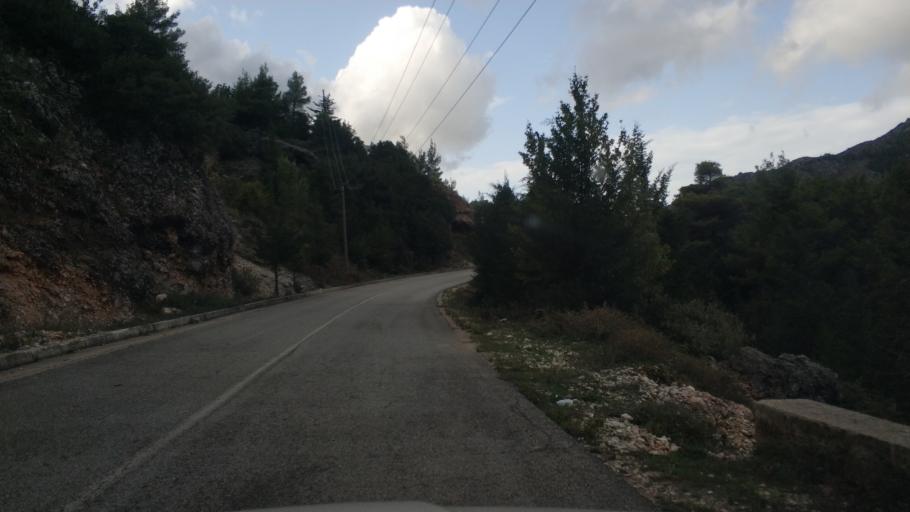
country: AL
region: Vlore
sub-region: Rrethi i Vlores
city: Orikum
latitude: 40.2497
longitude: 19.5425
